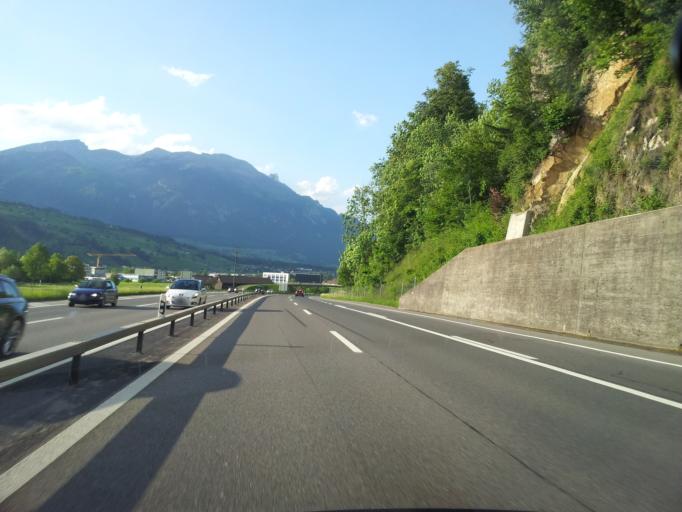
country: CH
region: Obwalden
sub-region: Obwalden
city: Sarnen
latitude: 46.8970
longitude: 8.2578
